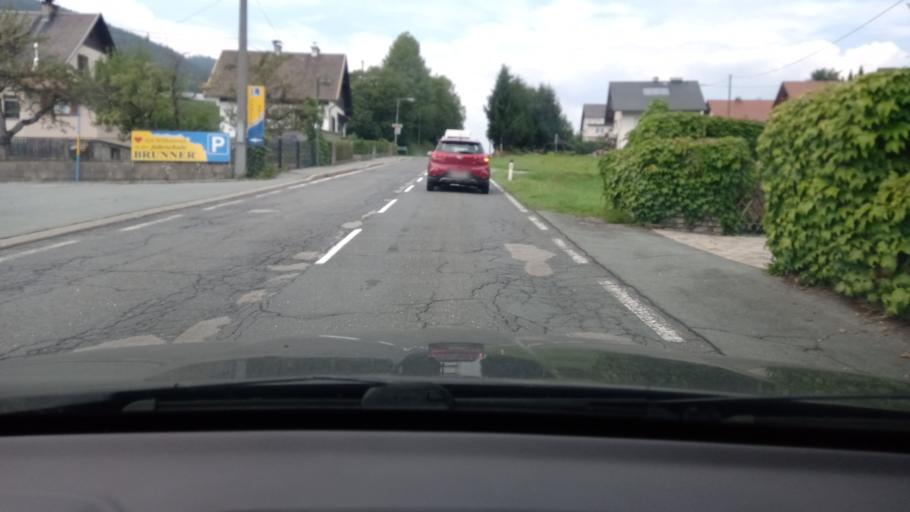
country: AT
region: Carinthia
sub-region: Politischer Bezirk Hermagor
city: Hermagor
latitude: 46.6289
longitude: 13.3609
